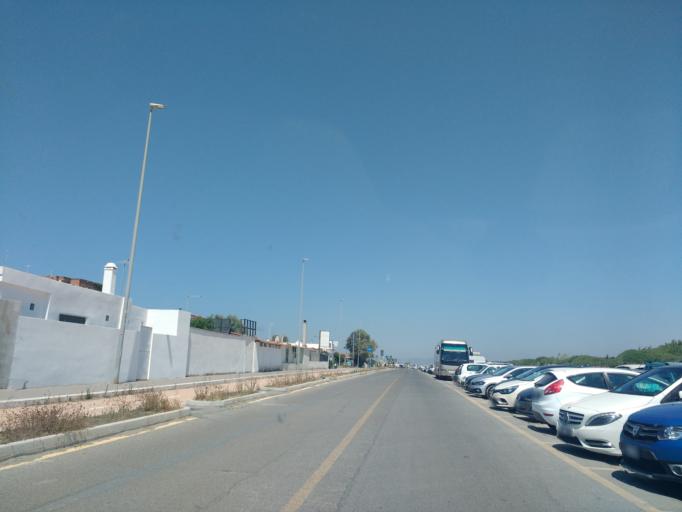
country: IT
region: Latium
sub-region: Citta metropolitana di Roma Capitale
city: Fregene
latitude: 41.8749
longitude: 12.1789
